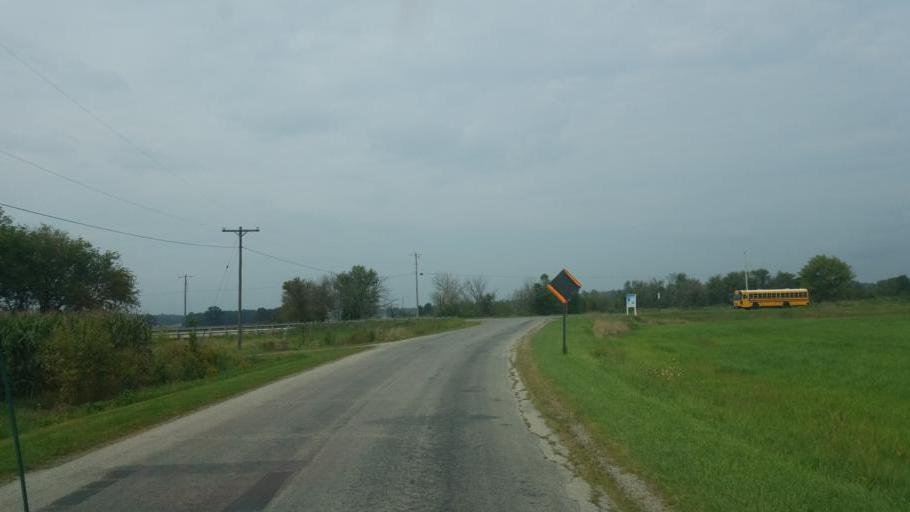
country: US
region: Ohio
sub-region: Wayne County
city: Rittman
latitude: 40.9449
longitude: -81.8120
